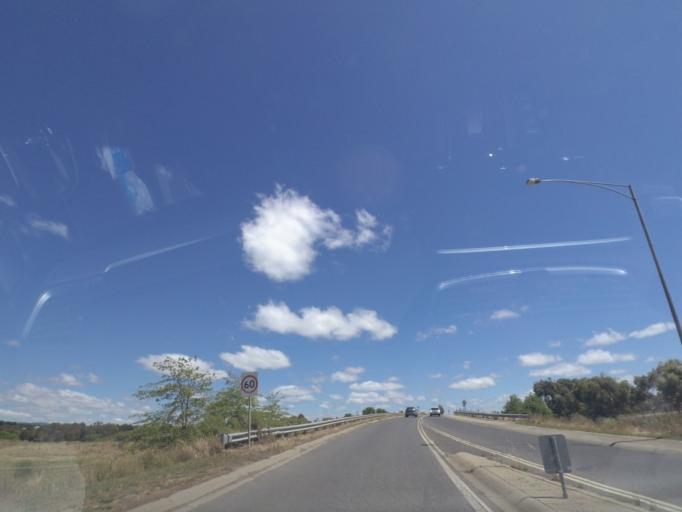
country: AU
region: Victoria
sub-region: Mount Alexander
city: Castlemaine
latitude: -37.2375
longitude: 144.4579
